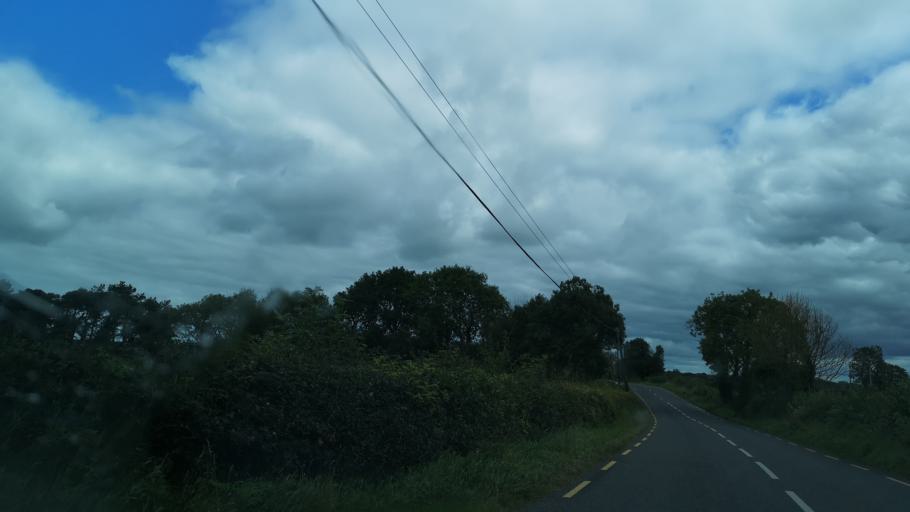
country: IE
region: Leinster
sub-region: Uibh Fhaili
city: Ferbane
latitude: 53.2247
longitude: -7.8496
